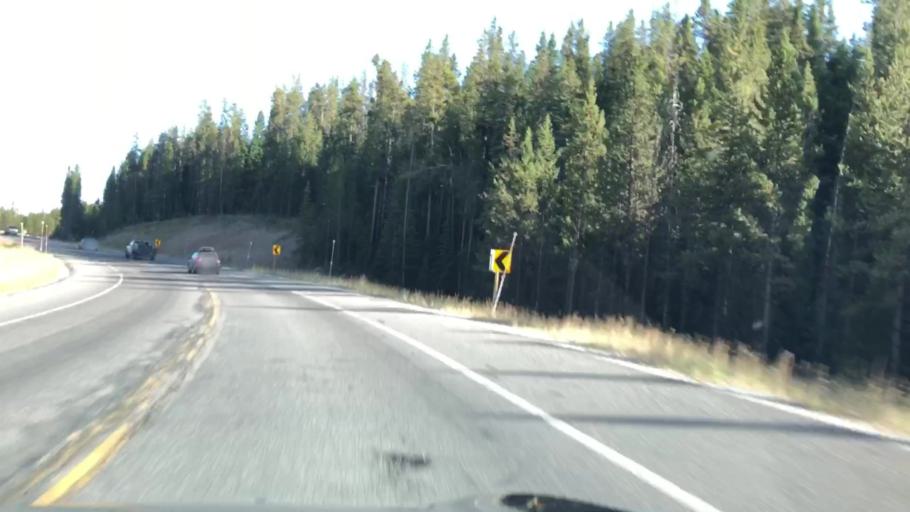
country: US
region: Montana
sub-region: Gallatin County
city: West Yellowstone
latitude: 44.8011
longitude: -111.1084
